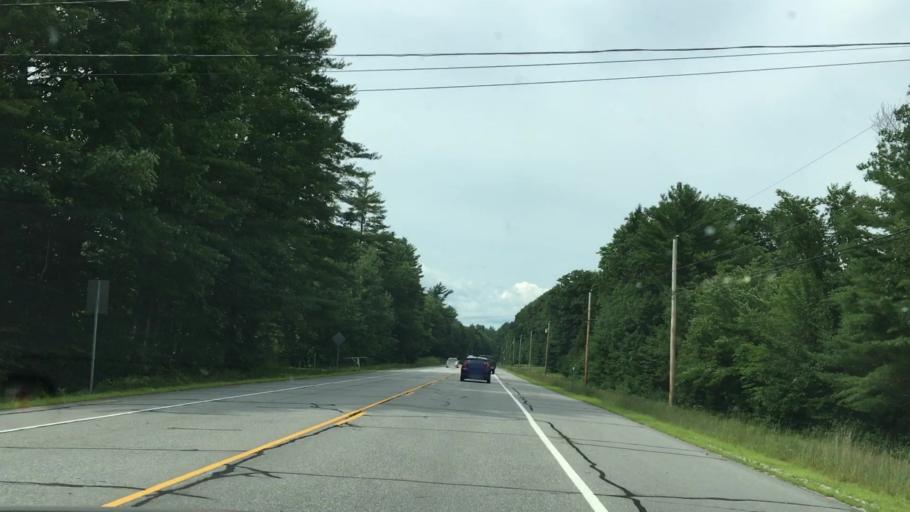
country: US
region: New Hampshire
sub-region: Hillsborough County
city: Hillsborough
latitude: 43.0858
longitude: -71.9181
